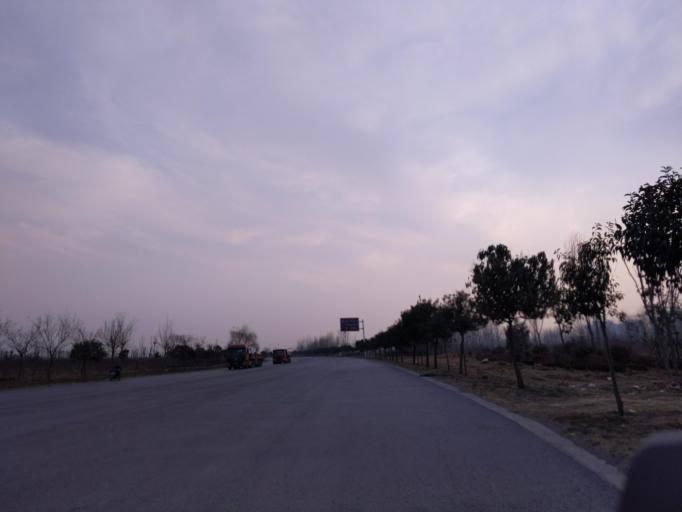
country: CN
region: Henan Sheng
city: Puyang
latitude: 35.8158
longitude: 114.9684
